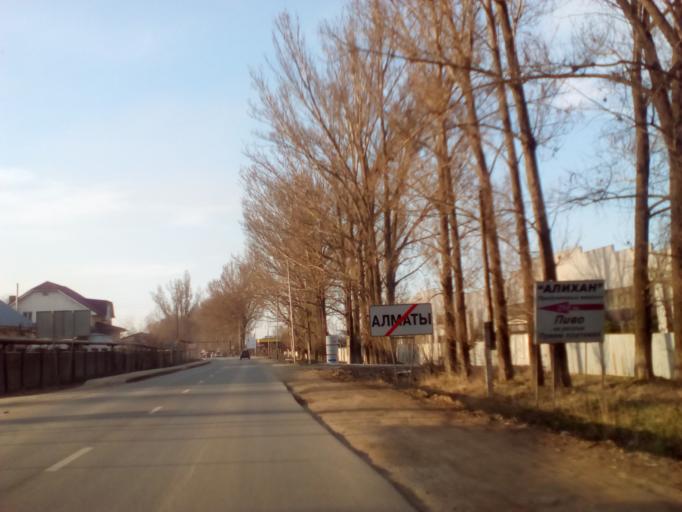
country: KZ
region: Almaty Oblysy
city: Burunday
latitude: 43.2512
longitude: 76.7838
